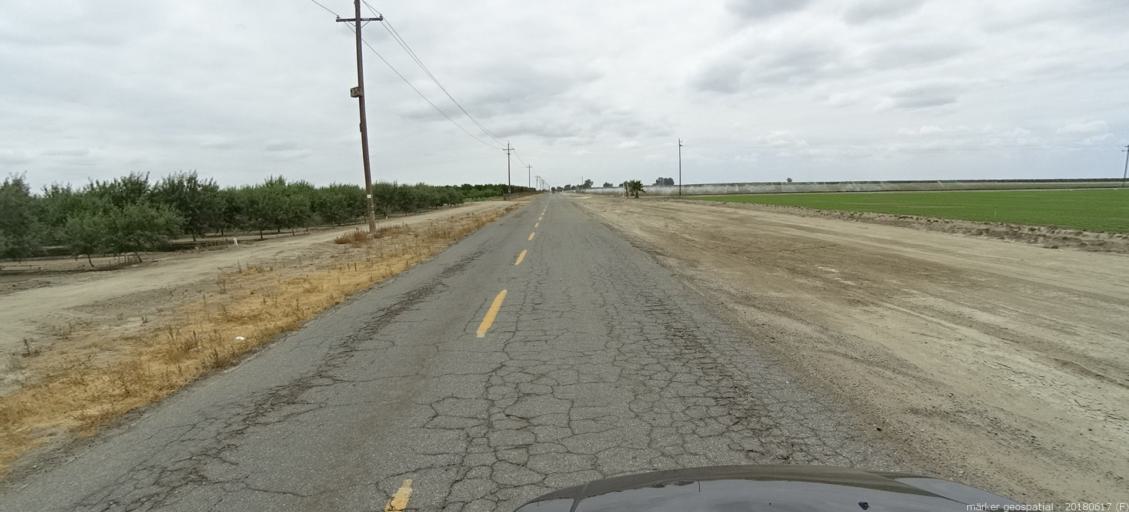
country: US
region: California
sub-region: Madera County
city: Madera
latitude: 36.9177
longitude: -120.1652
